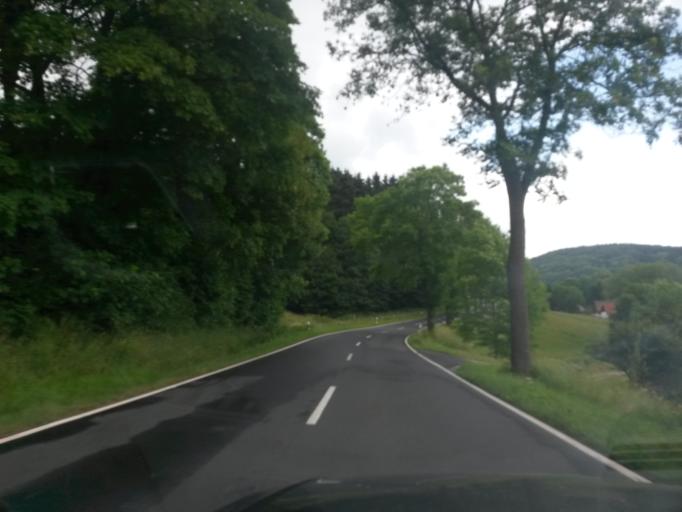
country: DE
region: Hesse
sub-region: Regierungsbezirk Kassel
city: Gersfeld
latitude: 50.4764
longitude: 9.9416
